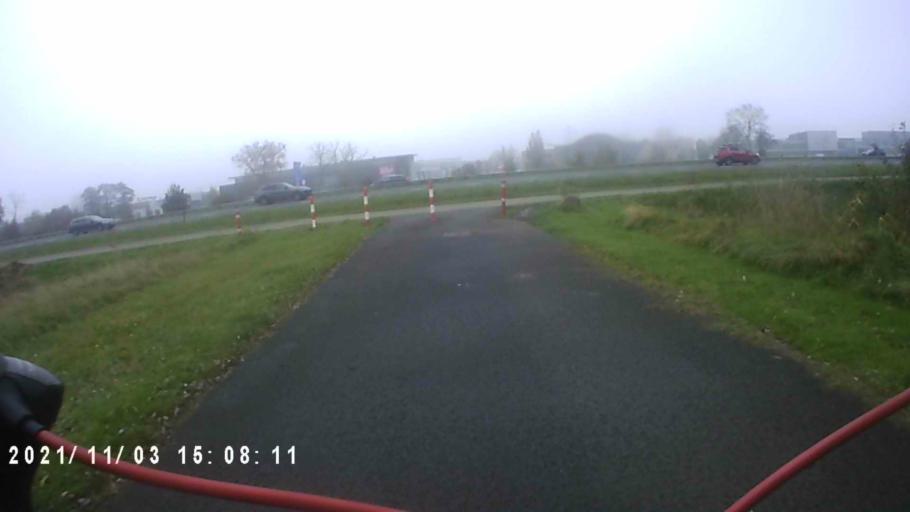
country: NL
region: Groningen
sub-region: Gemeente Leek
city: Leek
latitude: 53.1814
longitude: 6.3678
